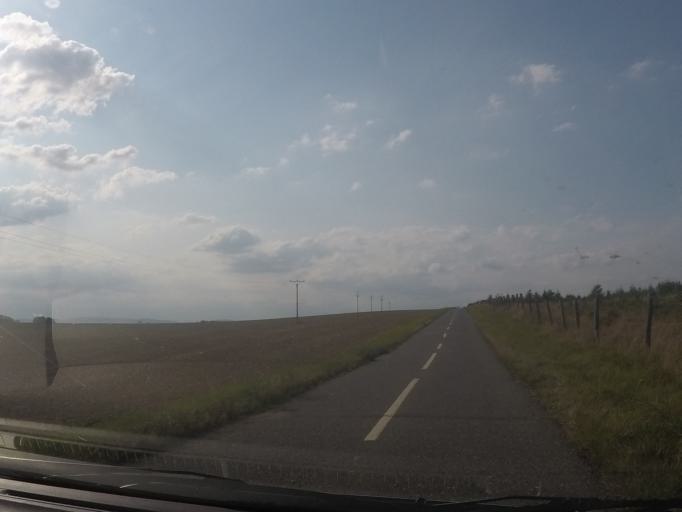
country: SK
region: Nitriansky
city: Levice
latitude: 48.2453
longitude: 18.6798
